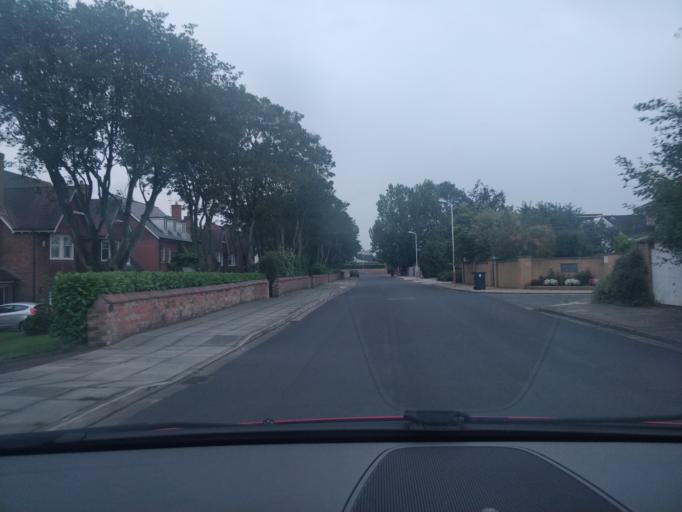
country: GB
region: England
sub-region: Sefton
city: Southport
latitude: 53.6316
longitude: -3.0327
